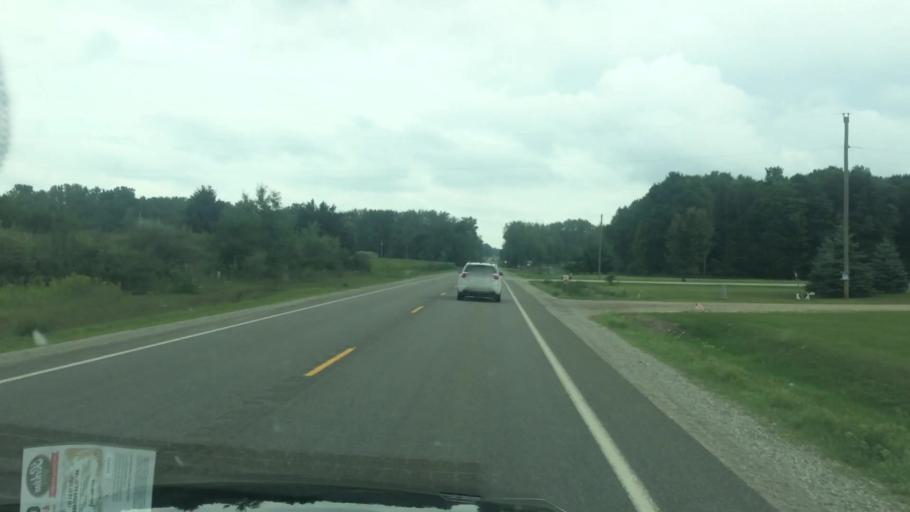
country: US
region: Michigan
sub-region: Tuscola County
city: Cass City
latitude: 43.6348
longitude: -83.0973
